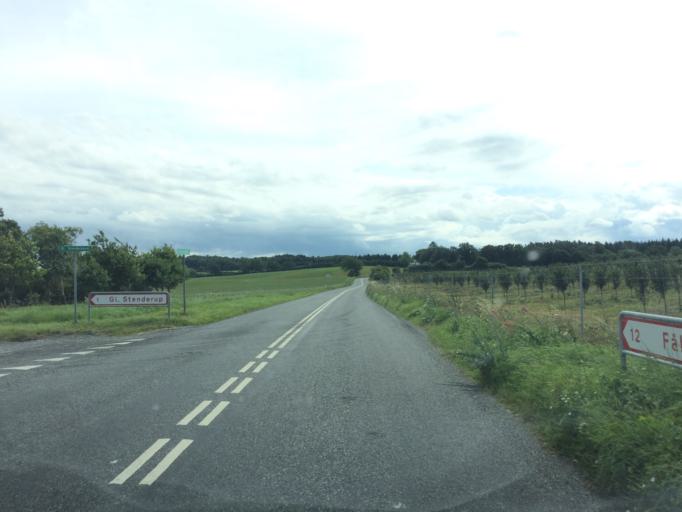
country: DK
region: South Denmark
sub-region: Faaborg-Midtfyn Kommune
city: Faaborg
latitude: 55.1861
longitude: 10.2474
